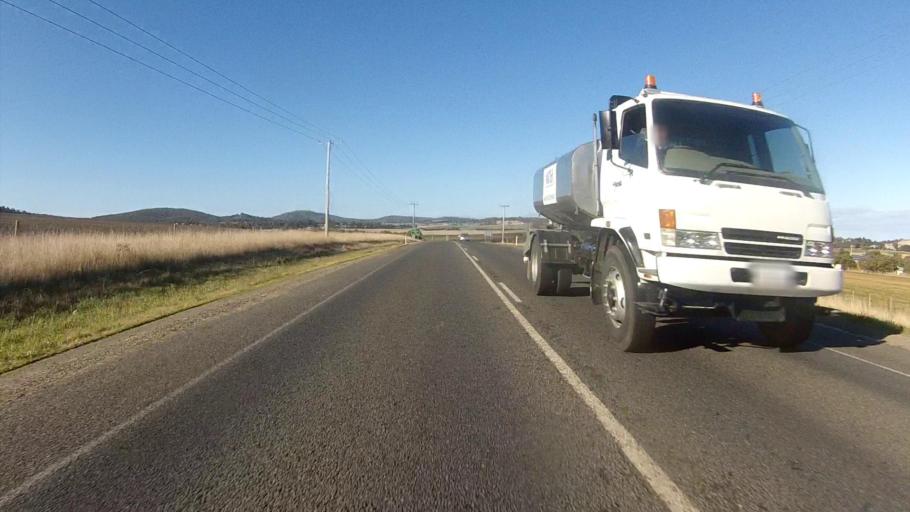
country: AU
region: Tasmania
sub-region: Sorell
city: Sorell
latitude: -42.7961
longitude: 147.6108
